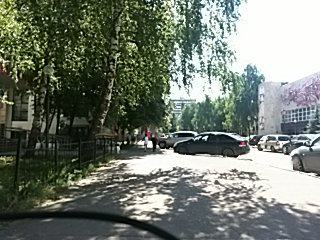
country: RU
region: Tatarstan
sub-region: Tukayevskiy Rayon
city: Naberezhnyye Chelny
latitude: 55.7464
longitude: 52.4156
